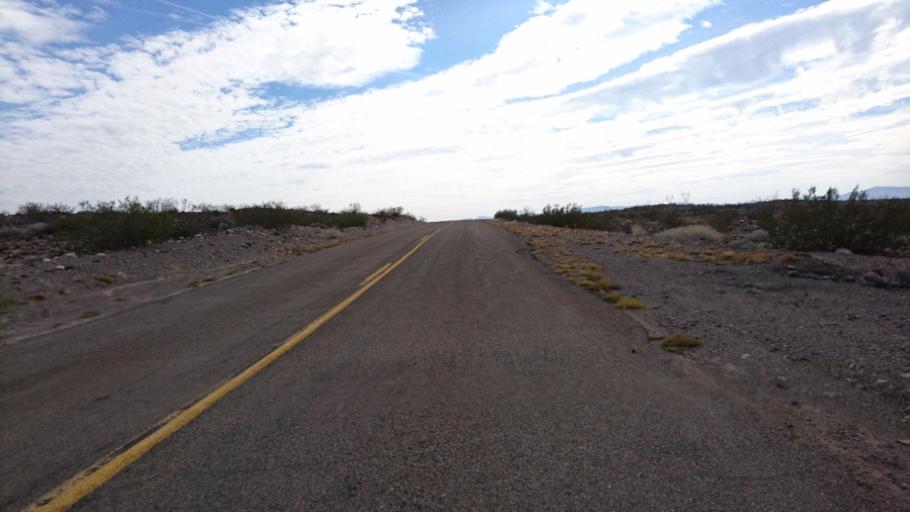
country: US
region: Arizona
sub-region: Mohave County
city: Mohave Valley
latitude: 34.8787
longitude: -114.4360
